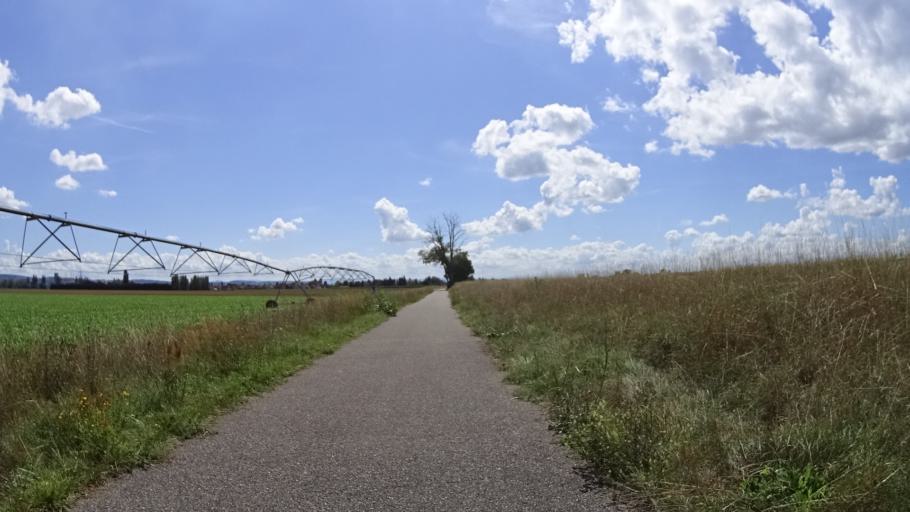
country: FR
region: Alsace
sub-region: Departement du Haut-Rhin
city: Ottmarsheim
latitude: 47.7991
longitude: 7.5052
